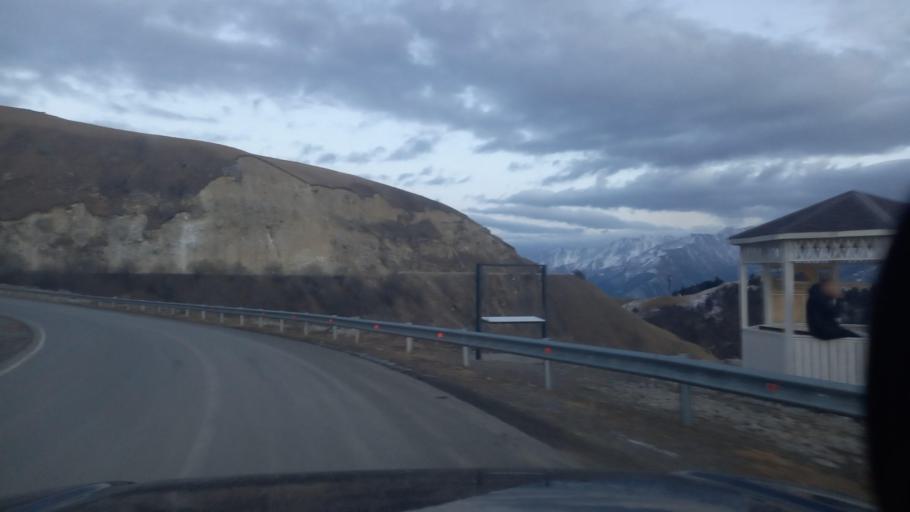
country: RU
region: Ingushetiya
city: Dzhayrakh
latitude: 42.8202
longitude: 44.8316
